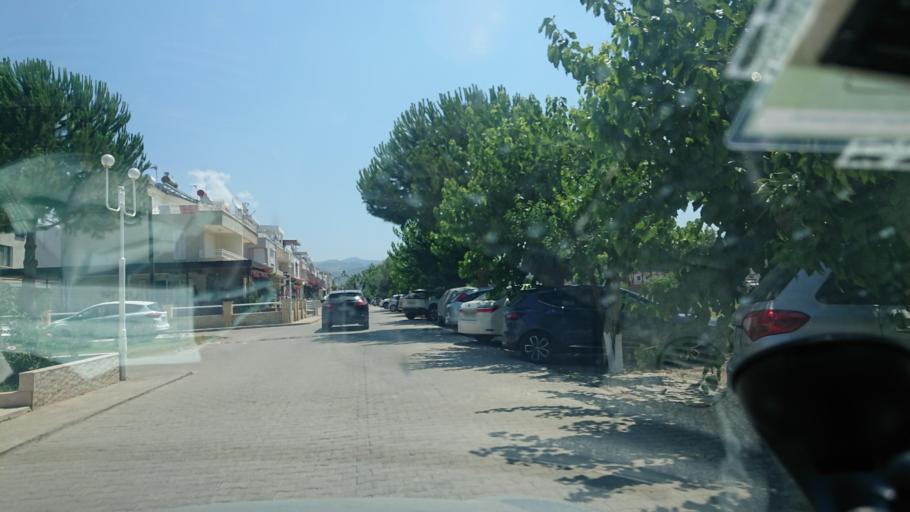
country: TR
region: Aydin
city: Kusadasi
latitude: 37.7982
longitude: 27.2717
